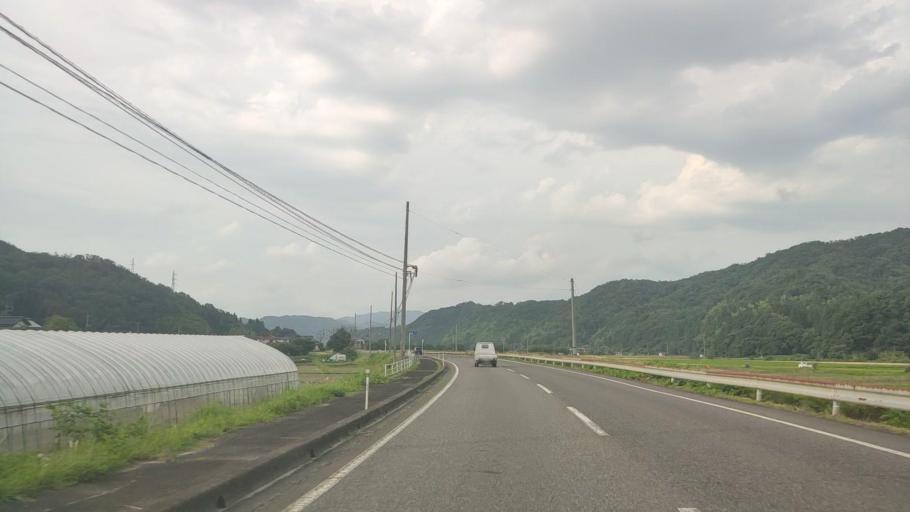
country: JP
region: Tottori
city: Kurayoshi
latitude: 35.3832
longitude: 133.8554
